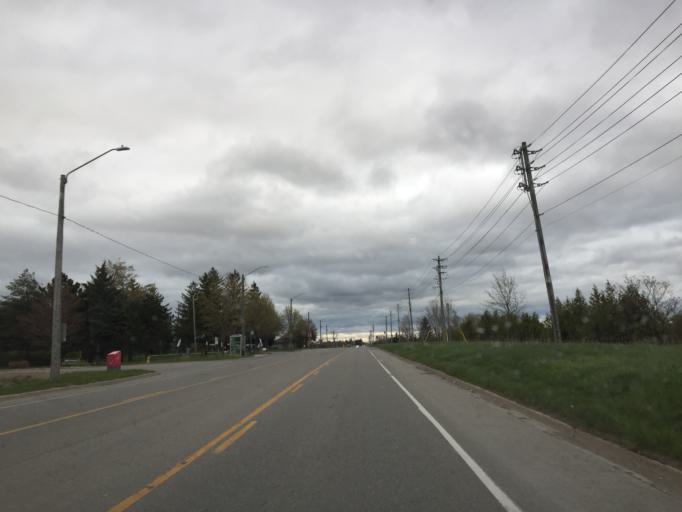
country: CA
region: Ontario
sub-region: Wellington County
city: Guelph
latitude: 43.5375
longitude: -80.3130
